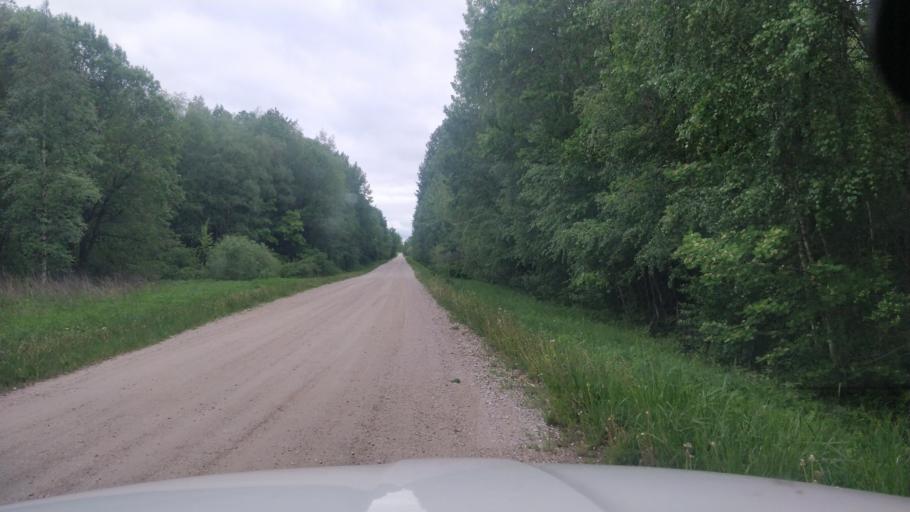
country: EE
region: Raplamaa
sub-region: Maerjamaa vald
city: Marjamaa
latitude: 58.7651
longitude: 24.2562
